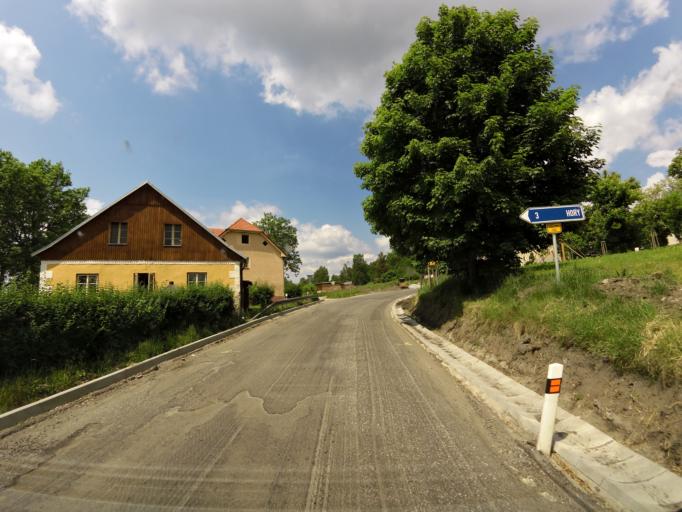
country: CZ
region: Jihocesky
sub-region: Okres Cesky Krumlov
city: Horni Plana
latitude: 48.7903
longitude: 13.9972
